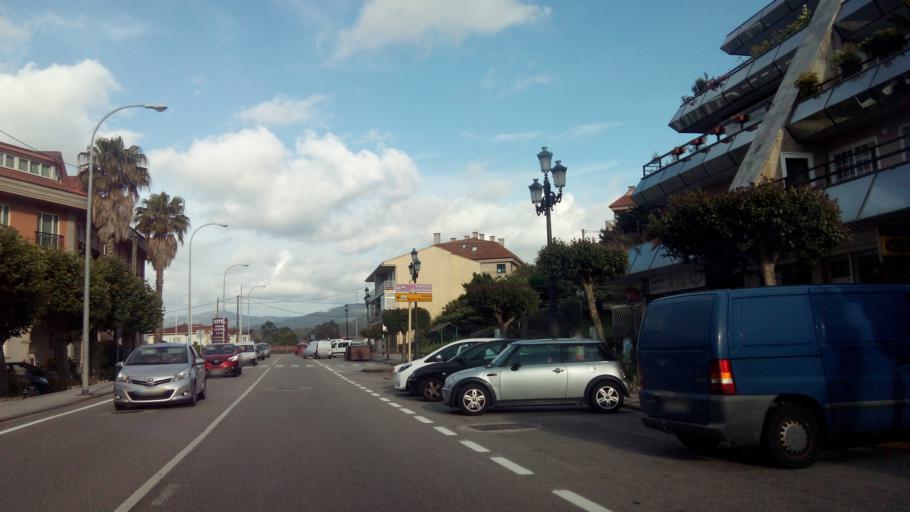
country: ES
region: Galicia
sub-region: Provincia de Pontevedra
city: Baiona
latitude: 42.1137
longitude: -8.8383
